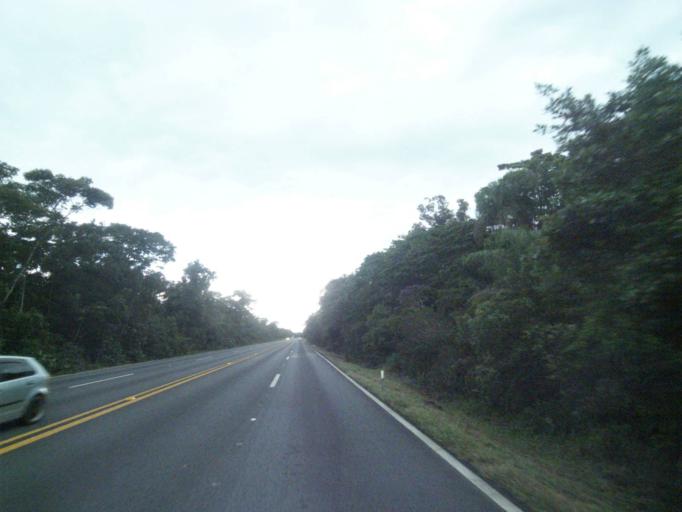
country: BR
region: Parana
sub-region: Guaratuba
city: Guaratuba
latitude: -25.7725
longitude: -48.5781
